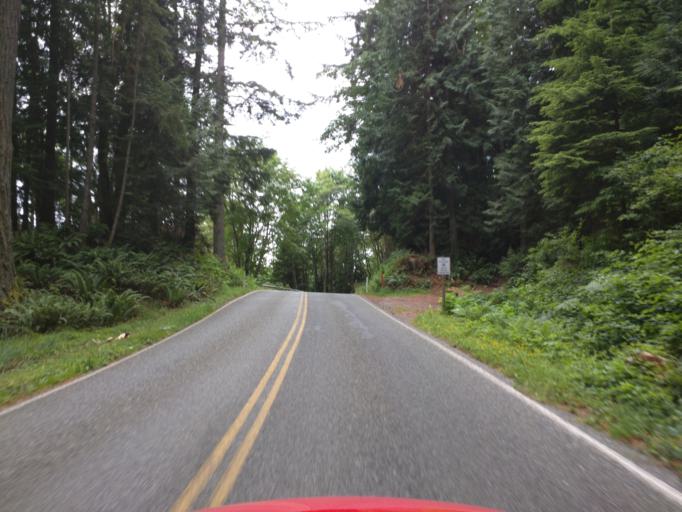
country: US
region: Washington
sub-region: Whatcom County
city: Sudden Valley
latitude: 48.6968
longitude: -122.3140
